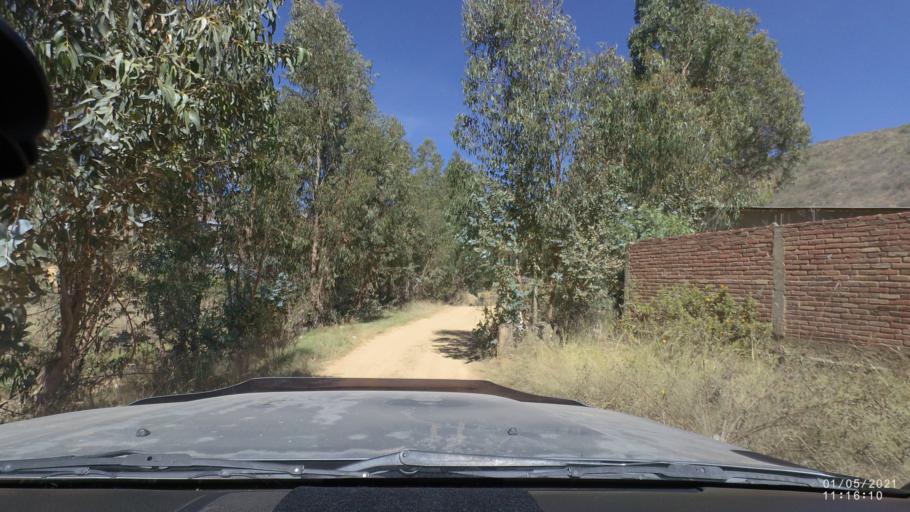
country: BO
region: Cochabamba
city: Tarata
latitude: -17.6383
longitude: -66.1139
